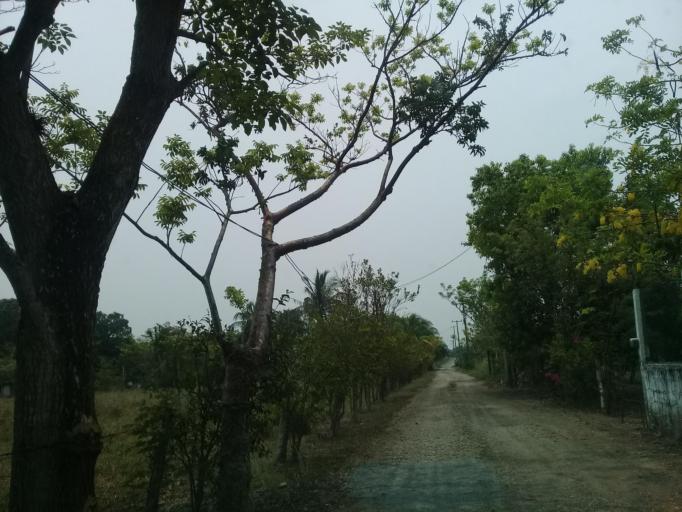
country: MX
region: Veracruz
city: Jamapa
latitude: 18.9585
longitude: -96.1942
